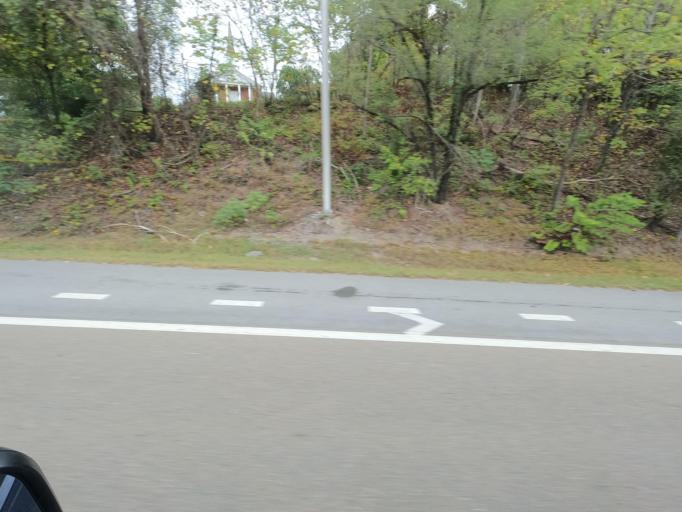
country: US
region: Tennessee
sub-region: Sullivan County
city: Kingsport
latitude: 36.5589
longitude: -82.5458
